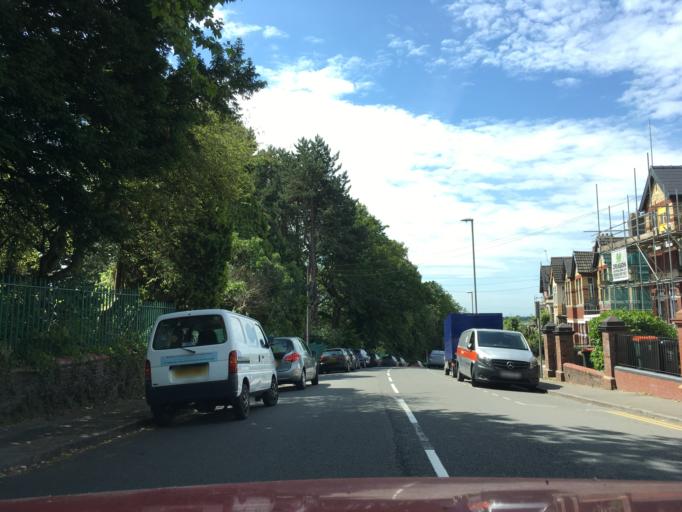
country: GB
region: Wales
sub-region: Newport
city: Newport
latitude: 51.5787
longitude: -3.0044
